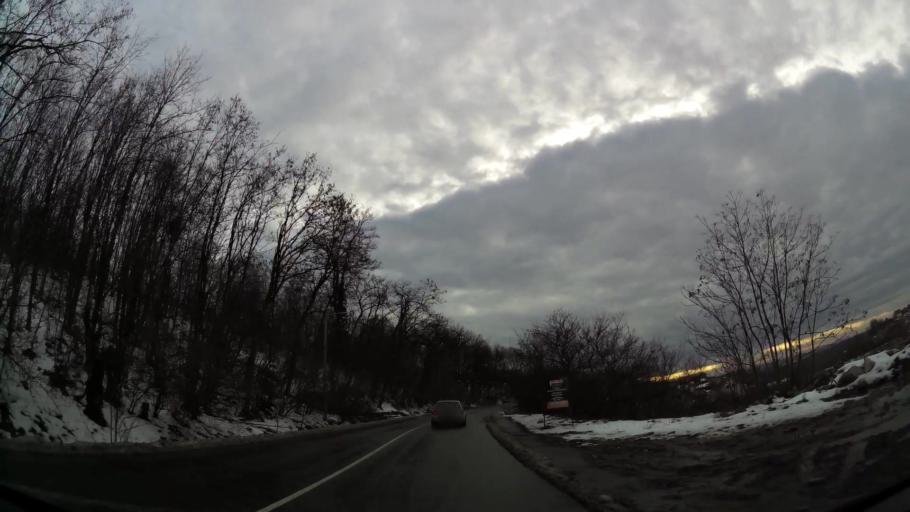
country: RS
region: Central Serbia
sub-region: Belgrade
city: Vozdovac
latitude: 44.7247
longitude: 20.4978
